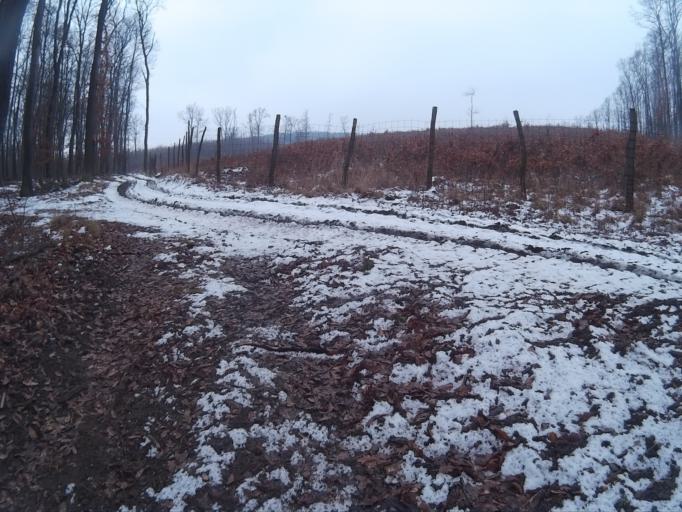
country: HU
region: Komarom-Esztergom
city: Tarjan
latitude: 47.5899
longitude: 18.5123
